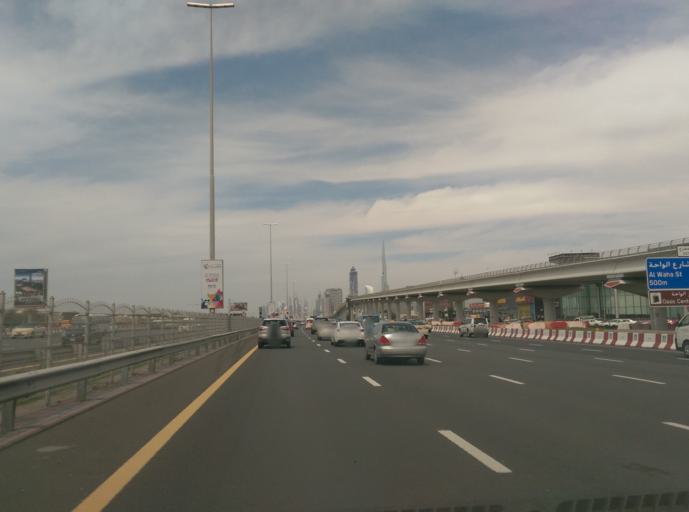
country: AE
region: Dubai
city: Dubai
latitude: 25.1603
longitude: 55.2311
